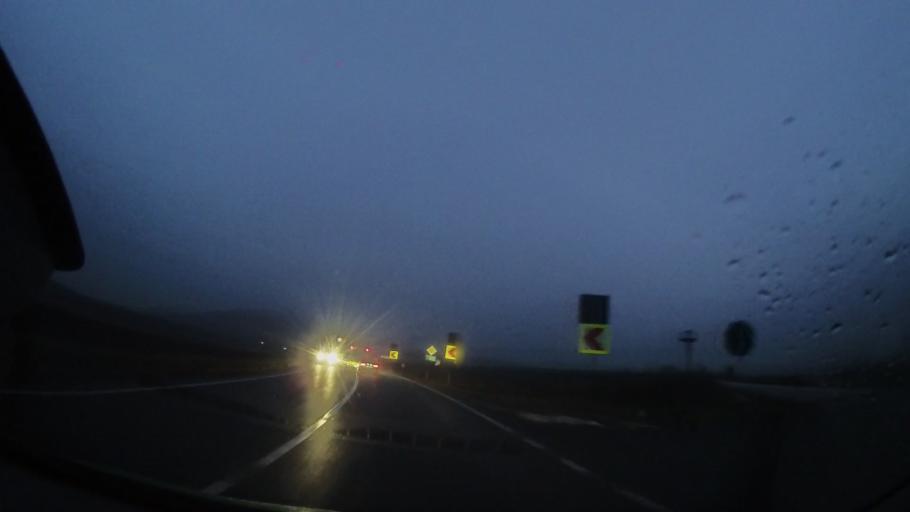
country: RO
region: Harghita
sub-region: Comuna Ditrau
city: Ditrau
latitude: 46.8321
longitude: 25.4923
